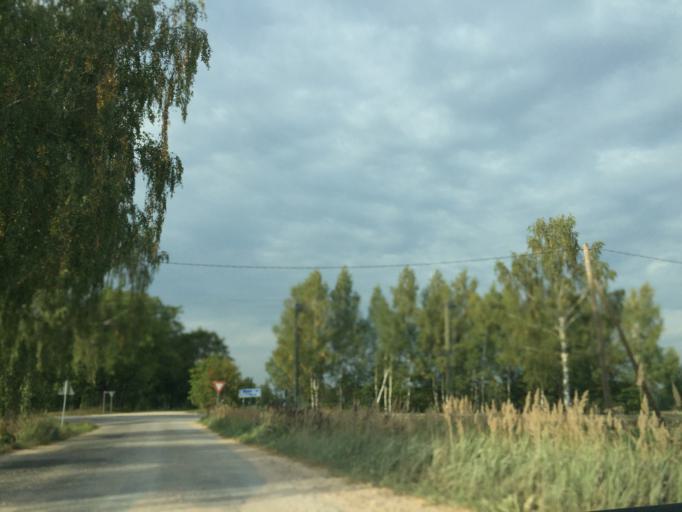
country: LV
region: Ikskile
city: Ikskile
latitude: 56.8197
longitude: 24.4488
